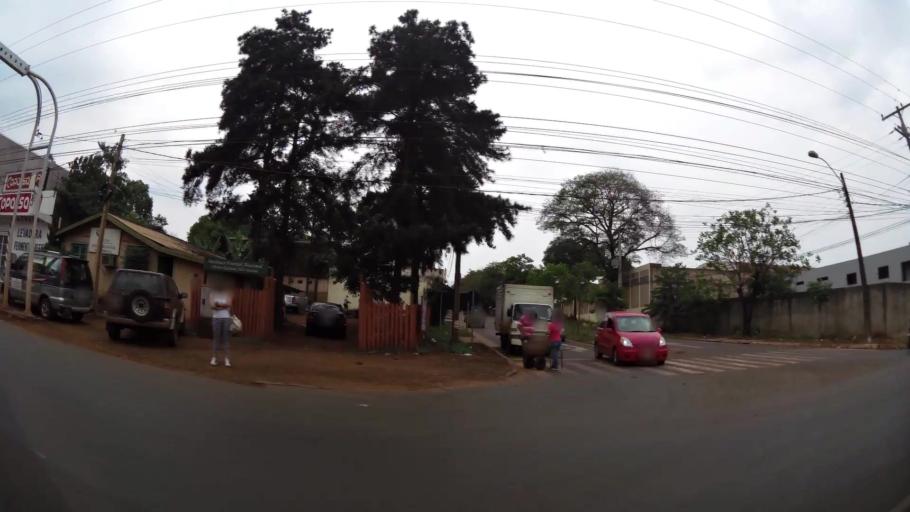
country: PY
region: Alto Parana
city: Ciudad del Este
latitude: -25.5061
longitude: -54.6431
